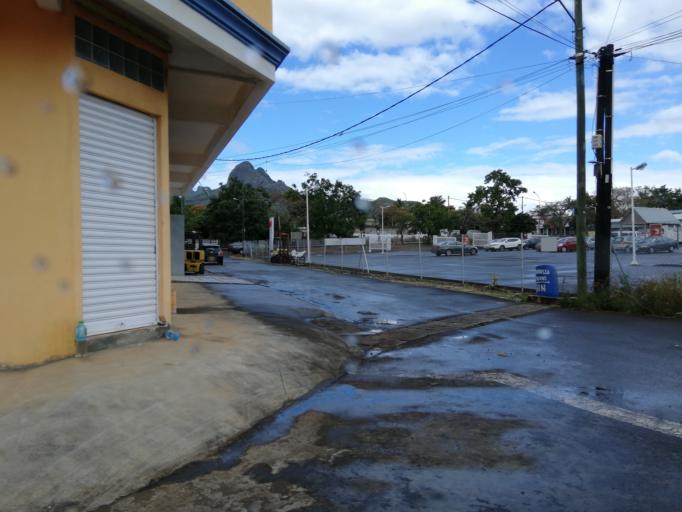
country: MU
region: Moka
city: Pailles
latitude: -20.2059
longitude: 57.4691
